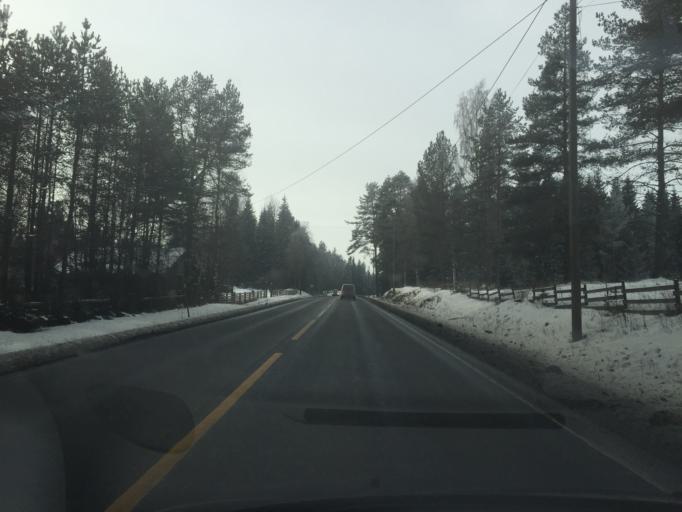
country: NO
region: Hedmark
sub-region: Elverum
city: Elverum
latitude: 60.8830
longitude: 11.5097
